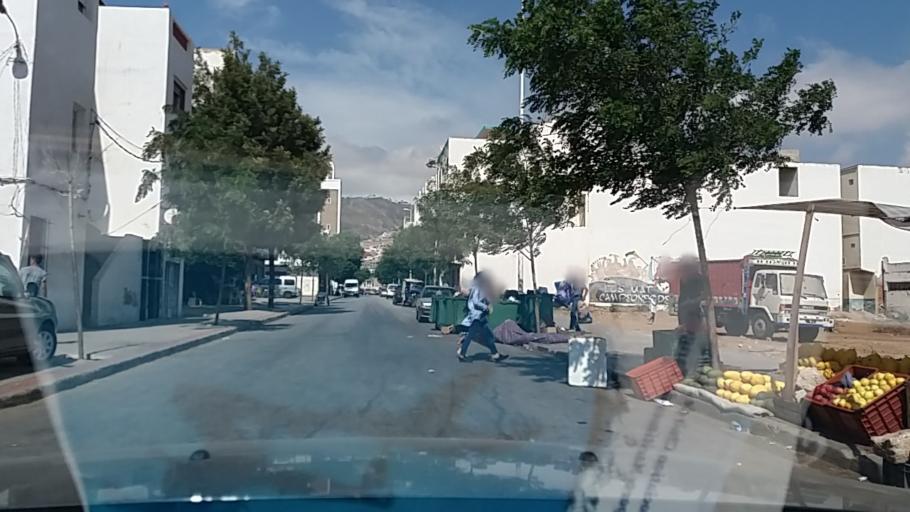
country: MA
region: Tanger-Tetouan
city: Tetouan
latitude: 35.5679
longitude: -5.4000
